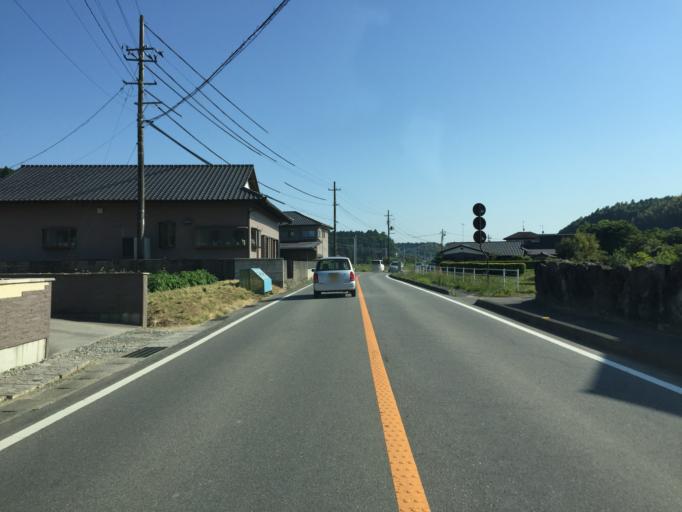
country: JP
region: Fukushima
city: Iwaki
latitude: 36.9345
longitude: 140.7979
